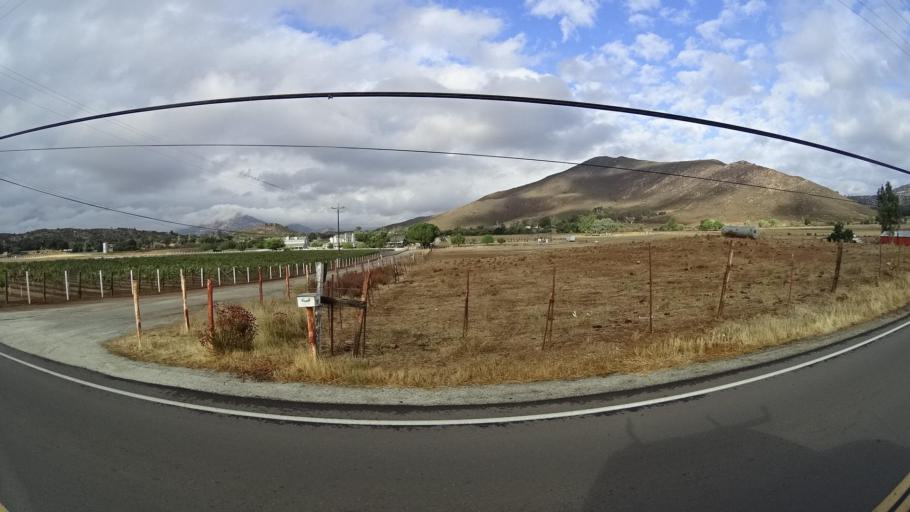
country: MX
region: Baja California
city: Tecate
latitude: 32.6130
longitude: -116.6133
